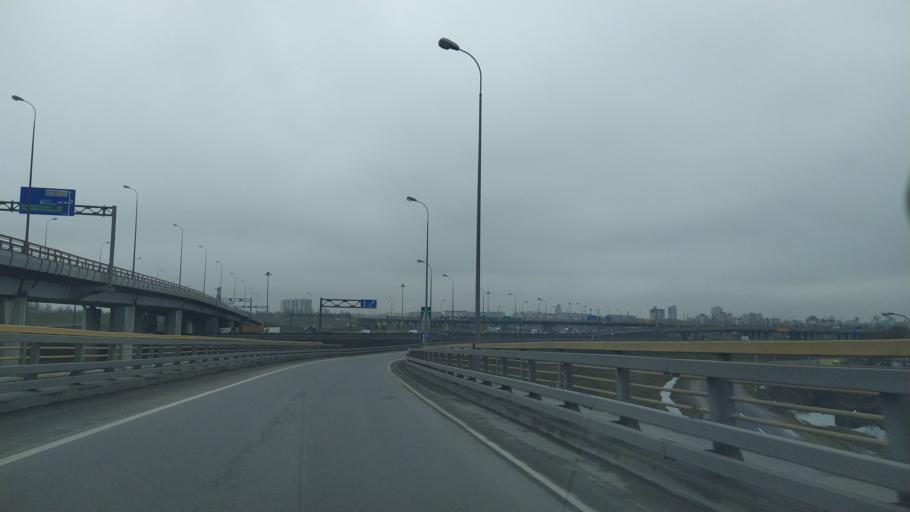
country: RU
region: St.-Petersburg
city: Dachnoye
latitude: 59.8323
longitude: 30.2882
